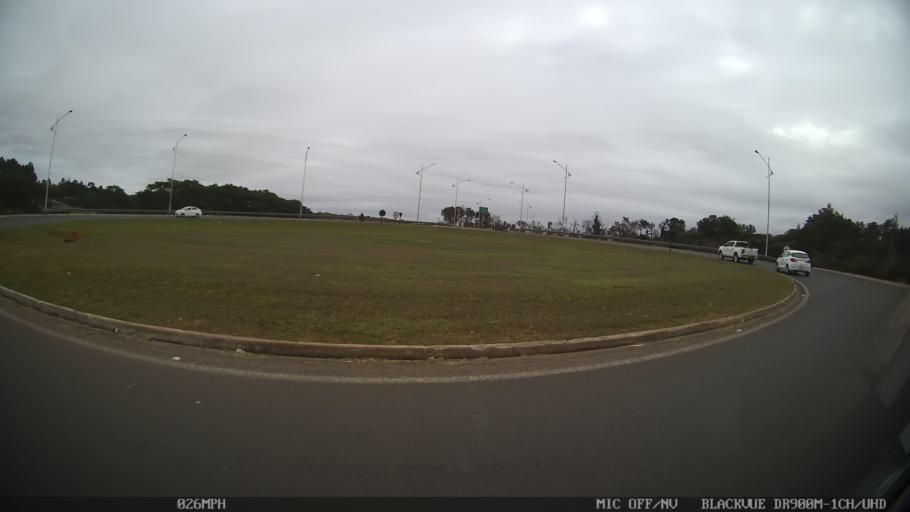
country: BR
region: Sao Paulo
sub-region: Sao Jose Do Rio Preto
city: Sao Jose do Rio Preto
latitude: -20.8200
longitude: -49.4341
